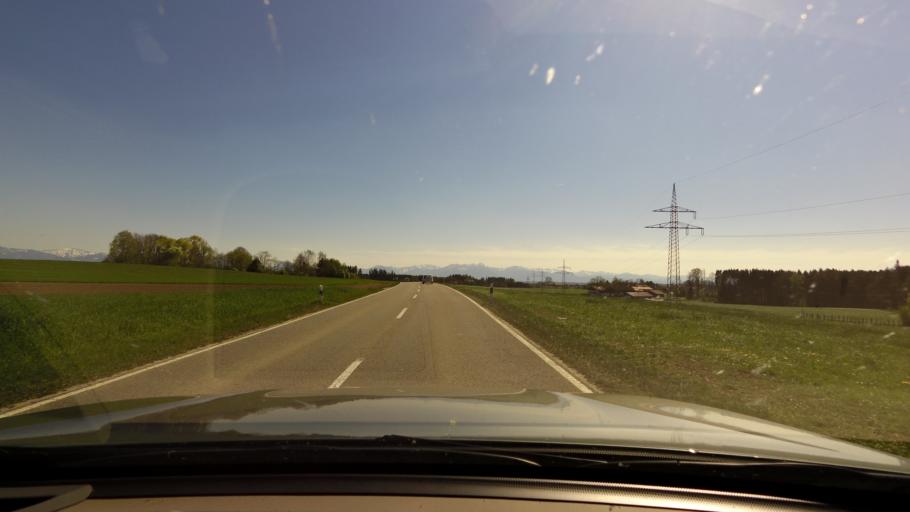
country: DE
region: Bavaria
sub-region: Upper Bavaria
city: Griesstatt
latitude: 47.9737
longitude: 12.1755
